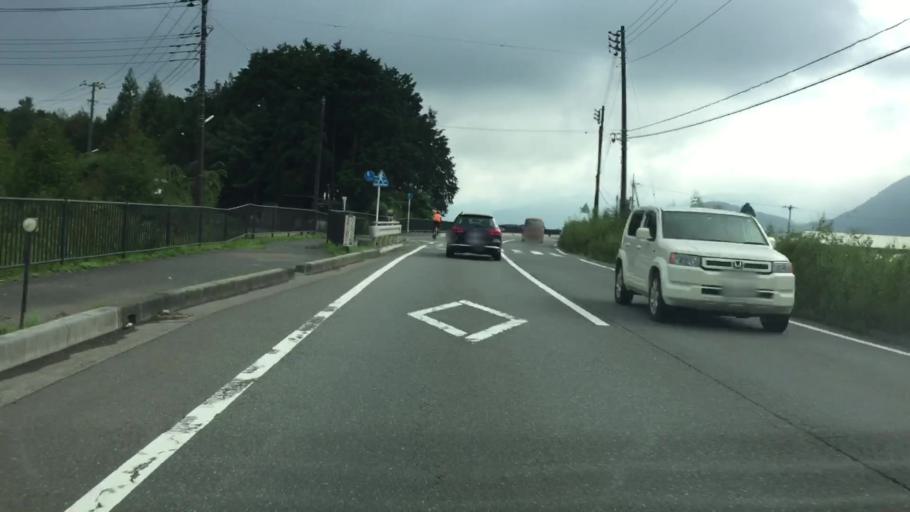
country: JP
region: Yamanashi
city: Fujikawaguchiko
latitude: 35.3988
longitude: 138.5806
